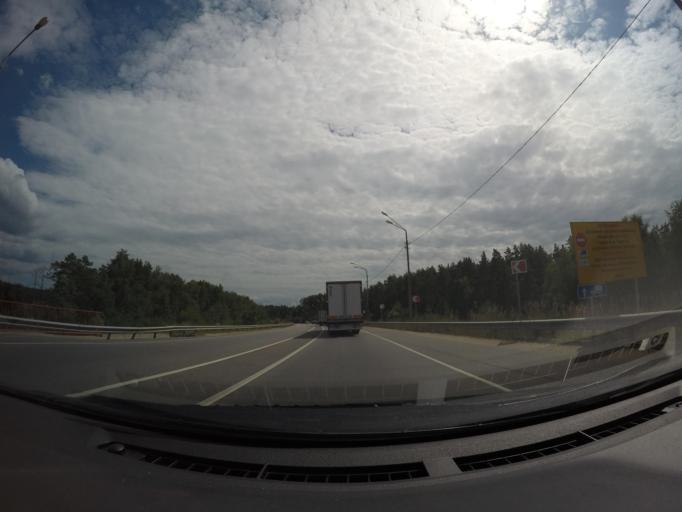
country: RU
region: Moskovskaya
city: Kratovo
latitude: 55.6377
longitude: 38.1845
